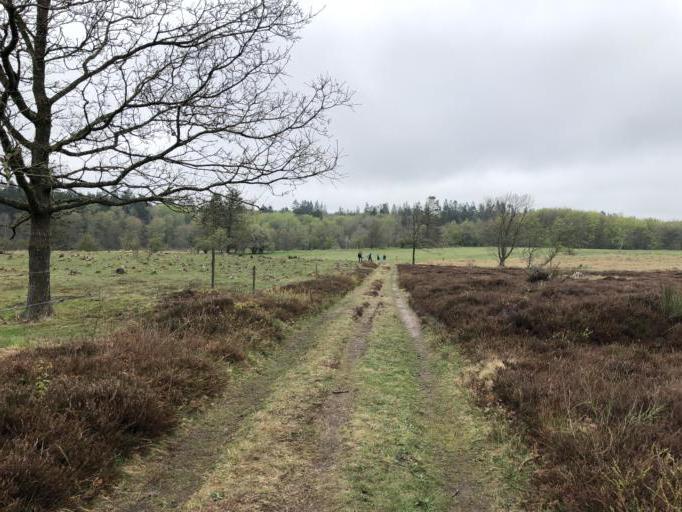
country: DK
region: Central Jutland
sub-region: Lemvig Kommune
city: Lemvig
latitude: 56.4820
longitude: 8.3609
